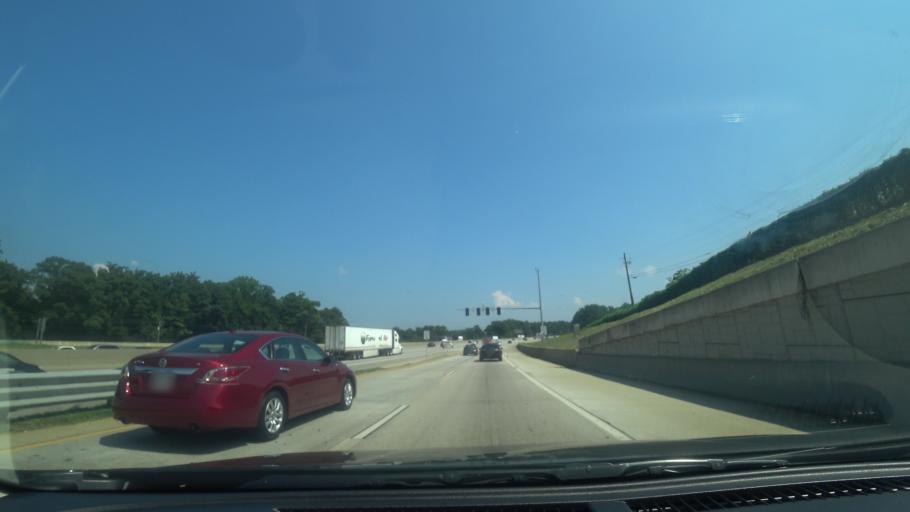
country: US
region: Georgia
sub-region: DeKalb County
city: Avondale Estates
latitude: 33.7759
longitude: -84.2387
